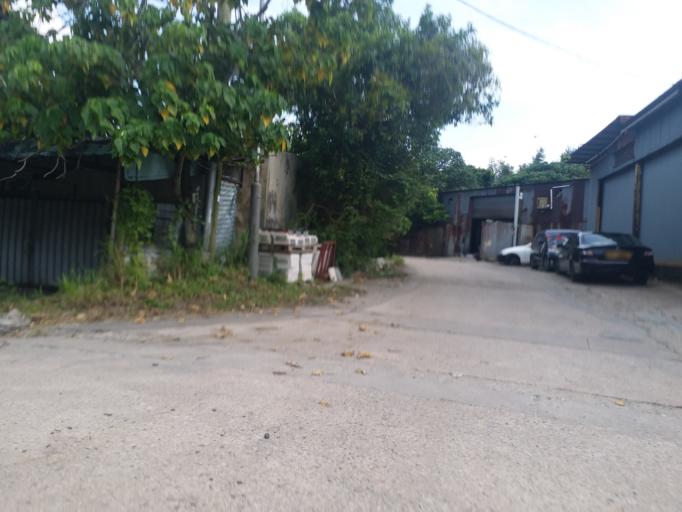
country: HK
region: Yuen Long
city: Yuen Long Kau Hui
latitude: 22.4411
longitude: 114.0018
